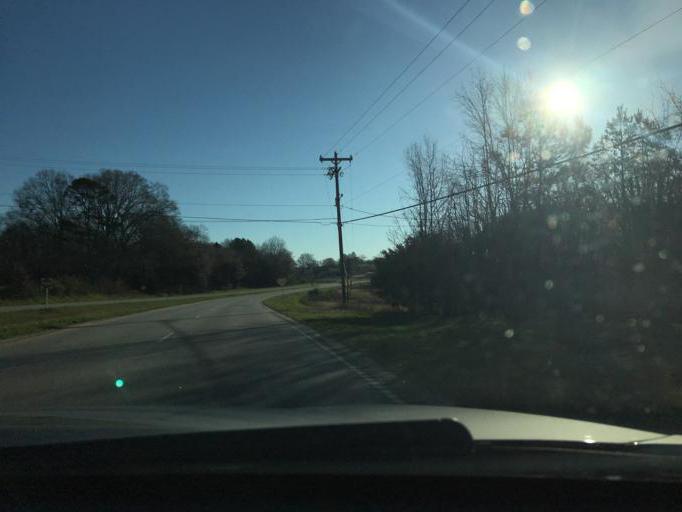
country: US
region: South Carolina
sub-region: Laurens County
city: Clinton
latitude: 34.4717
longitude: -81.9177
